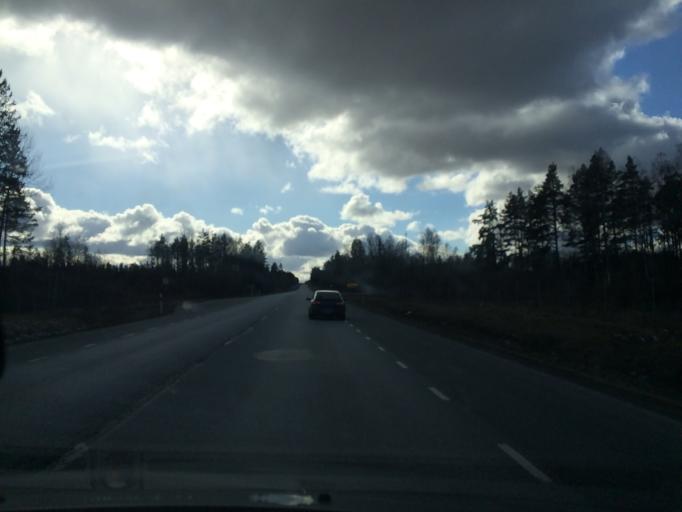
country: SE
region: Vaestra Goetaland
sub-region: Mariestads Kommun
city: Mariestad
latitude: 58.6223
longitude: 13.6662
